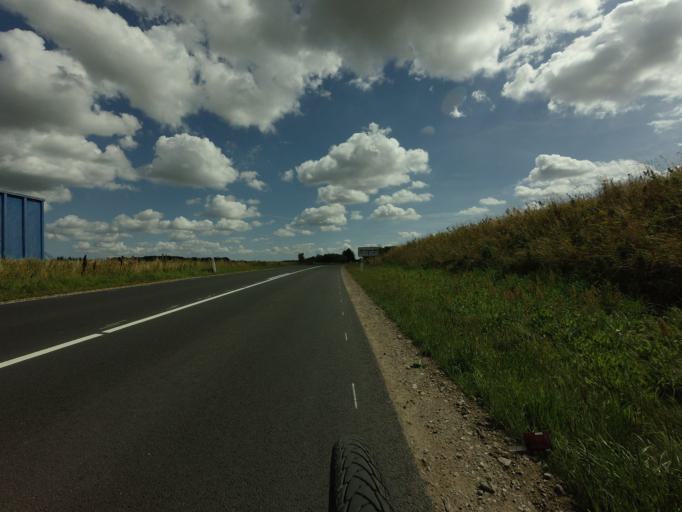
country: DK
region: North Denmark
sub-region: Hjorring Kommune
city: Hjorring
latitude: 57.4530
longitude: 9.9142
